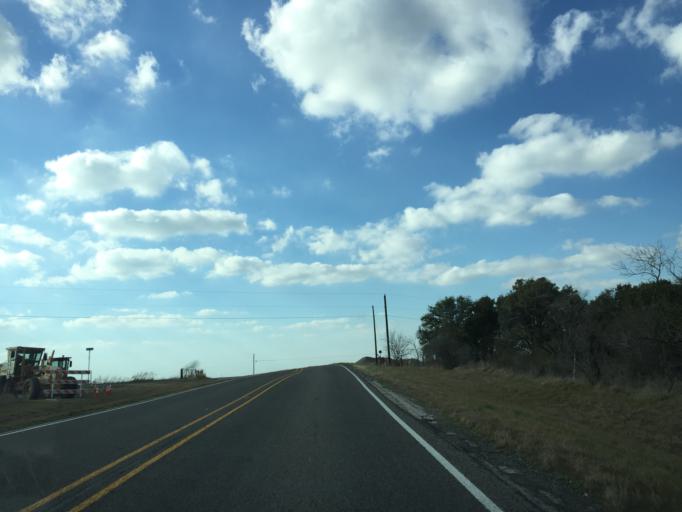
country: US
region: Texas
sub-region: Williamson County
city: Taylor
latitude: 30.6386
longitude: -97.4201
